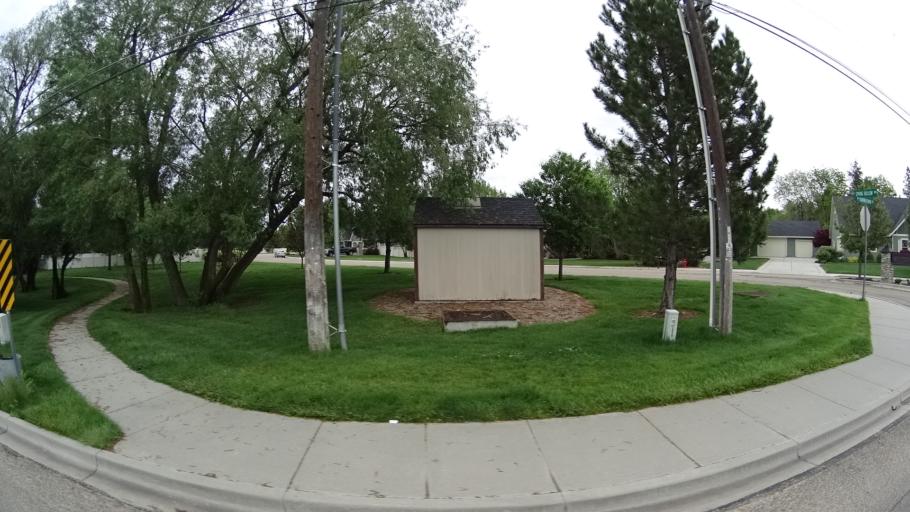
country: US
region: Idaho
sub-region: Ada County
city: Star
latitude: 43.7066
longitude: -116.4899
